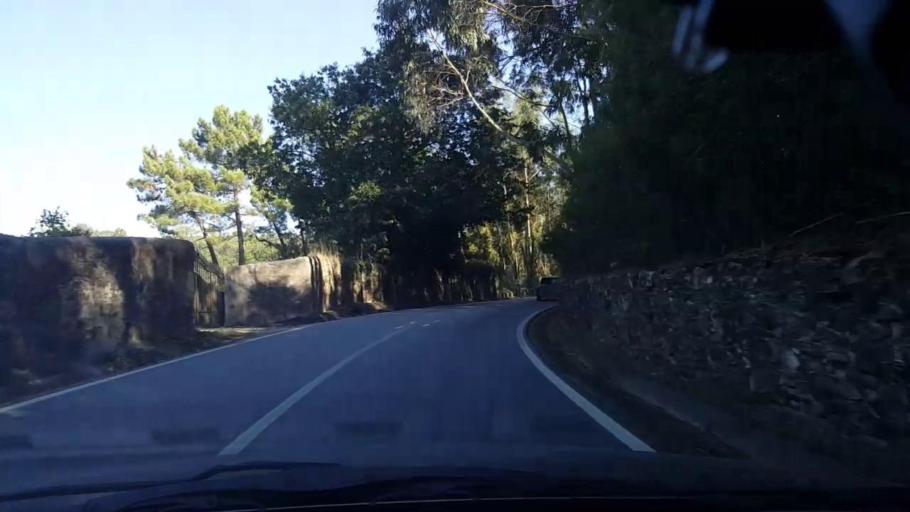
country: PT
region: Porto
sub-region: Maia
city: Gemunde
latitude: 41.3250
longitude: -8.6479
